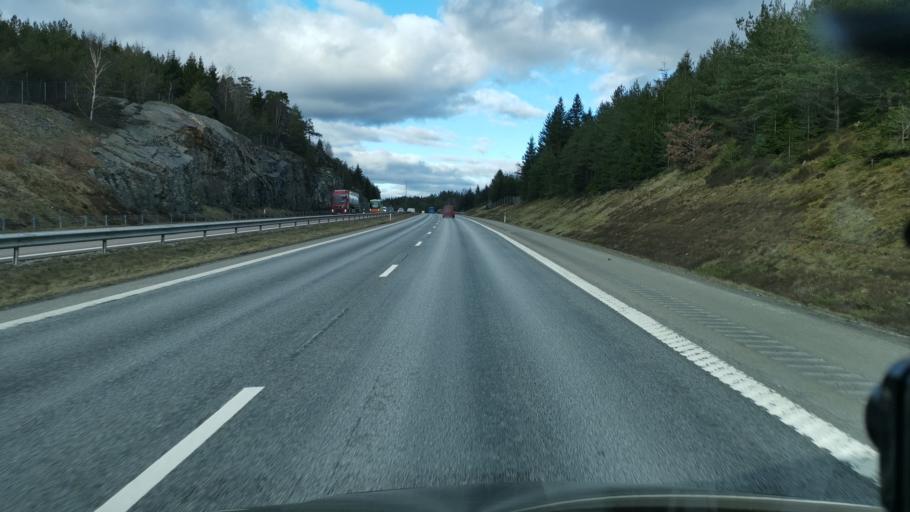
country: SE
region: Vaestra Goetaland
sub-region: Uddevalla Kommun
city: Ljungskile
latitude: 58.1734
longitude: 11.9003
